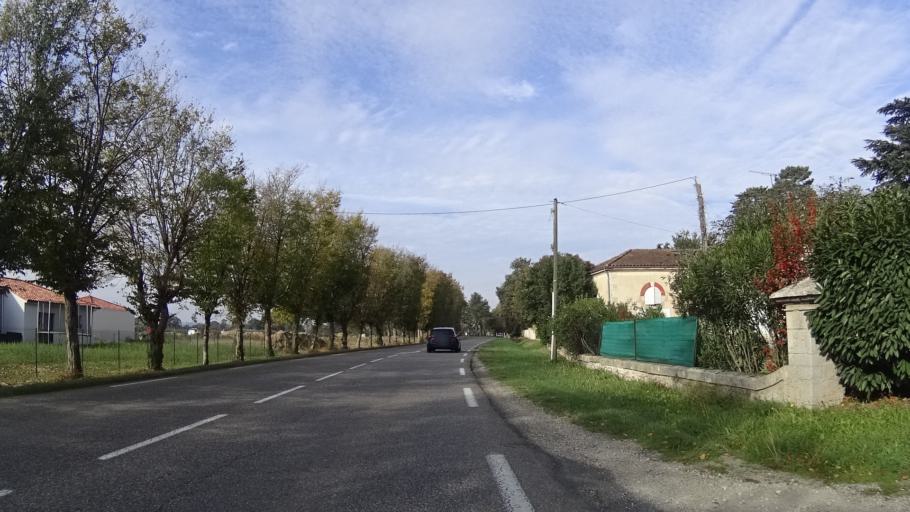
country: FR
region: Aquitaine
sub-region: Departement du Lot-et-Garonne
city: Brax
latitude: 44.2048
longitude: 0.5443
